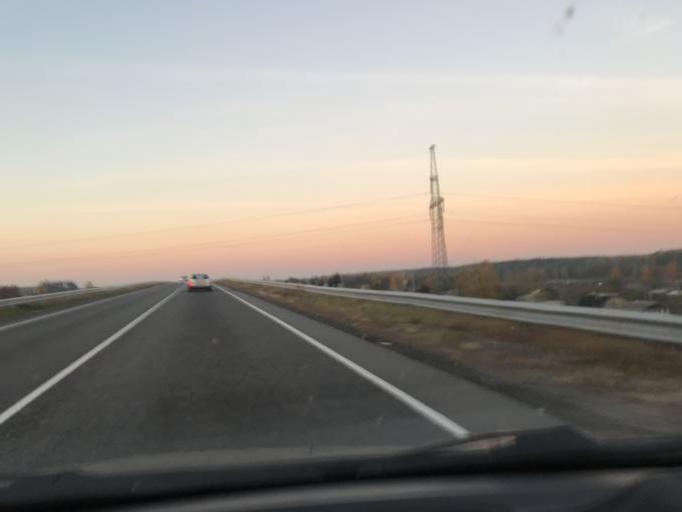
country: BY
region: Mogilev
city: Babruysk
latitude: 53.1778
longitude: 29.0456
